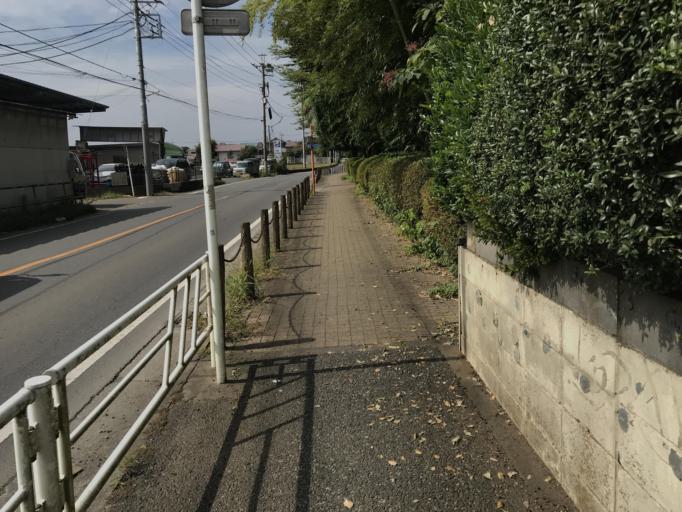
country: JP
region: Tokyo
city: Tanashicho
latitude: 35.7775
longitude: 139.5511
